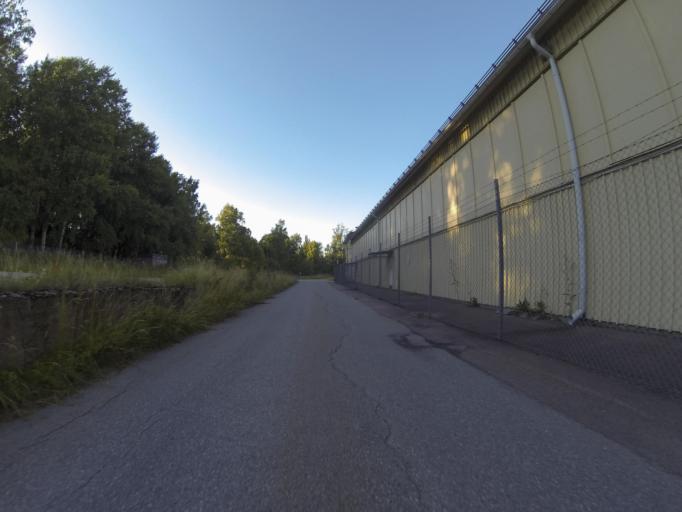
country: SE
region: Vaestmanland
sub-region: Vasteras
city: Vasteras
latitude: 59.5818
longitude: 16.6251
